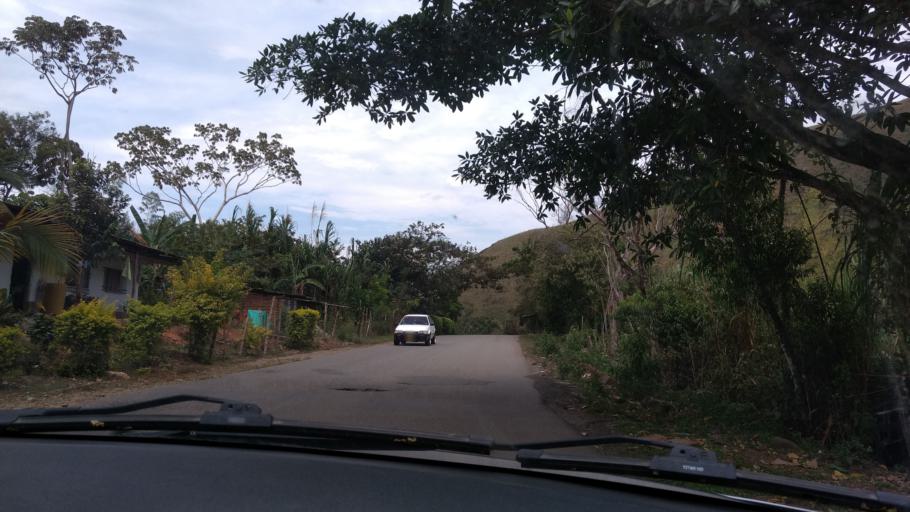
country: CO
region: Cauca
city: Buenos Aires
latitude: 3.0349
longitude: -76.6737
